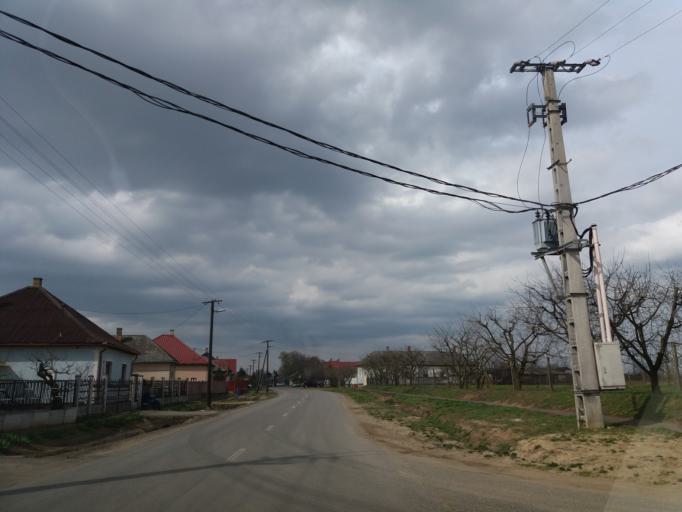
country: HU
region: Szabolcs-Szatmar-Bereg
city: Nyirtass
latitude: 48.1047
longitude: 22.0276
